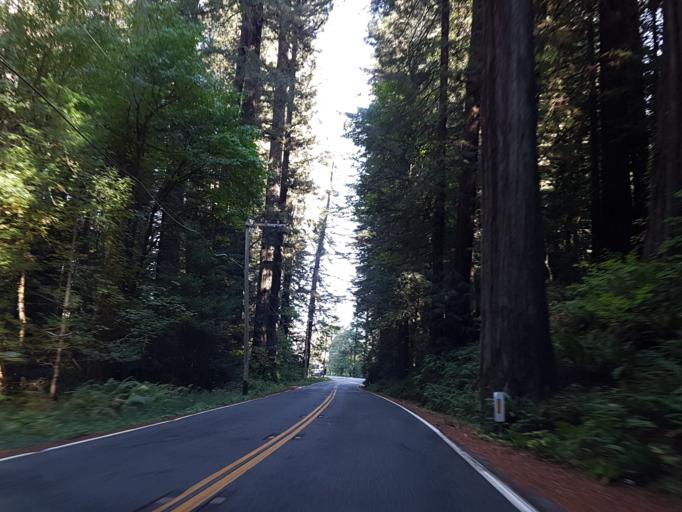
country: US
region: California
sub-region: Humboldt County
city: Rio Dell
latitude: 40.4162
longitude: -123.9695
